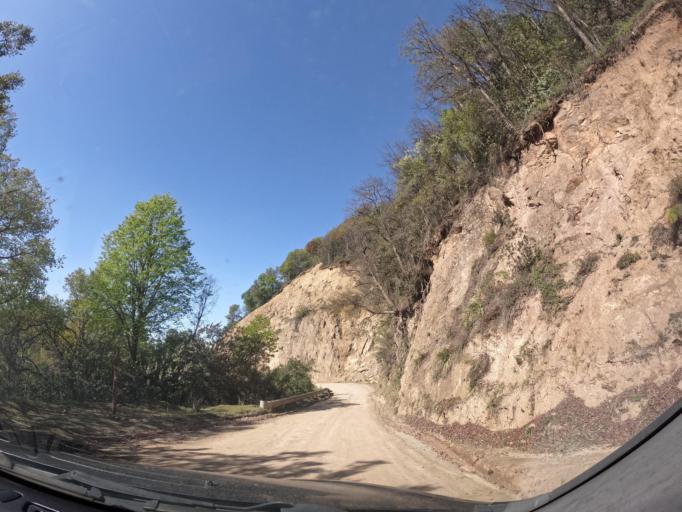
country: CL
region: Maule
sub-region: Provincia de Linares
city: Longavi
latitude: -36.2430
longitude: -71.4374
